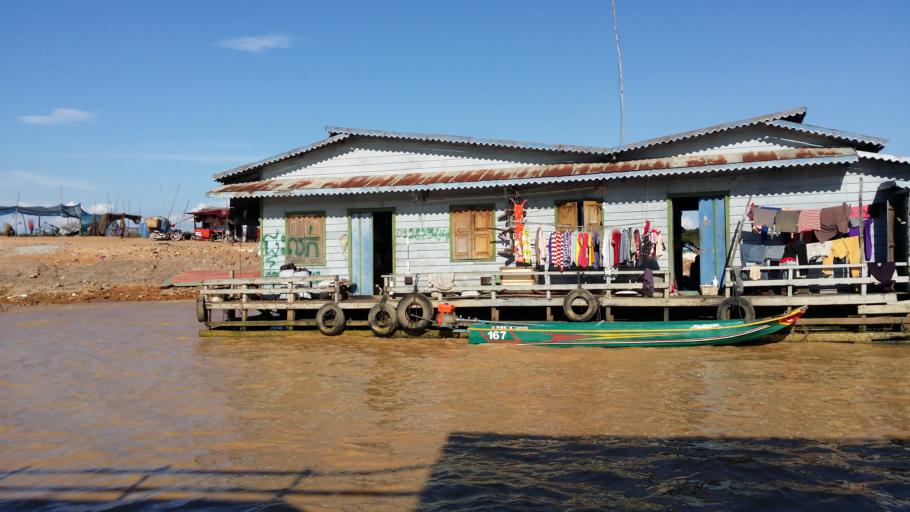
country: KH
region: Siem Reap
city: Siem Reap
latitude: 13.2546
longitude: 103.8229
